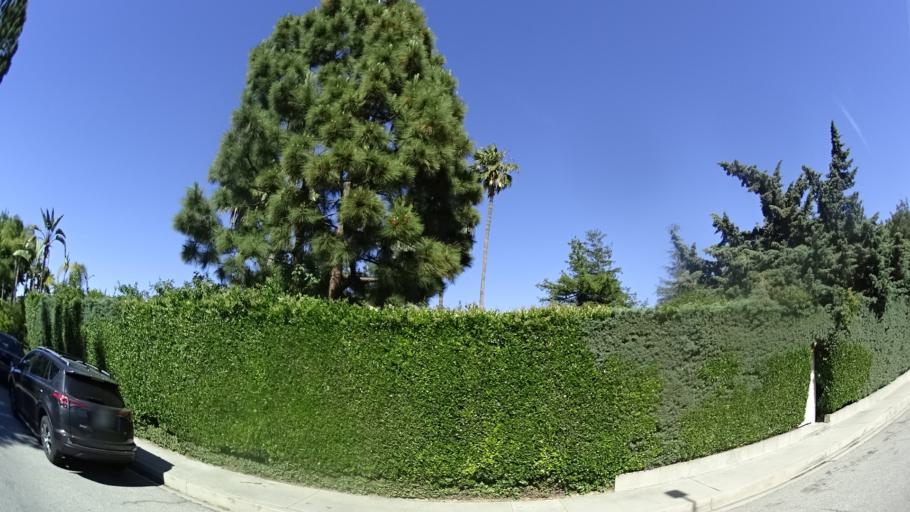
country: US
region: California
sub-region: Los Angeles County
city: Sherman Oaks
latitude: 34.1410
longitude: -118.4516
